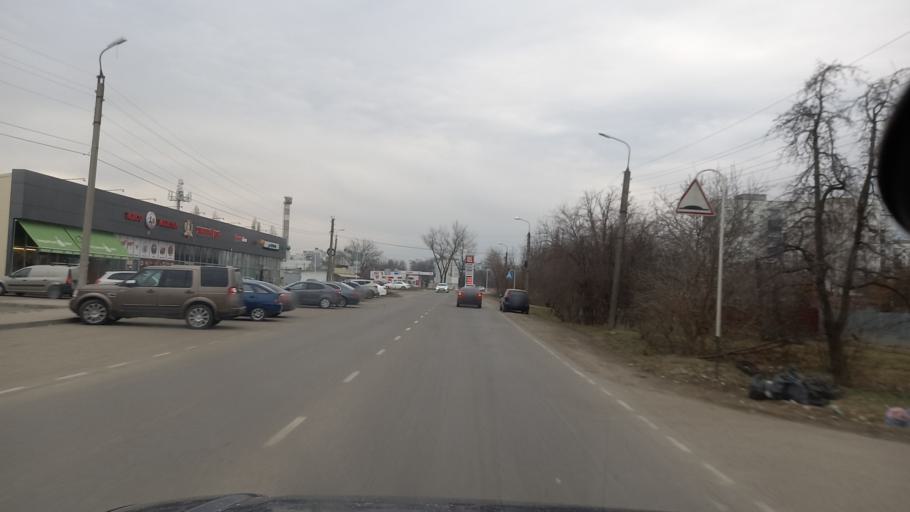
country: RU
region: Adygeya
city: Maykop
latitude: 44.5810
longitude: 40.1354
